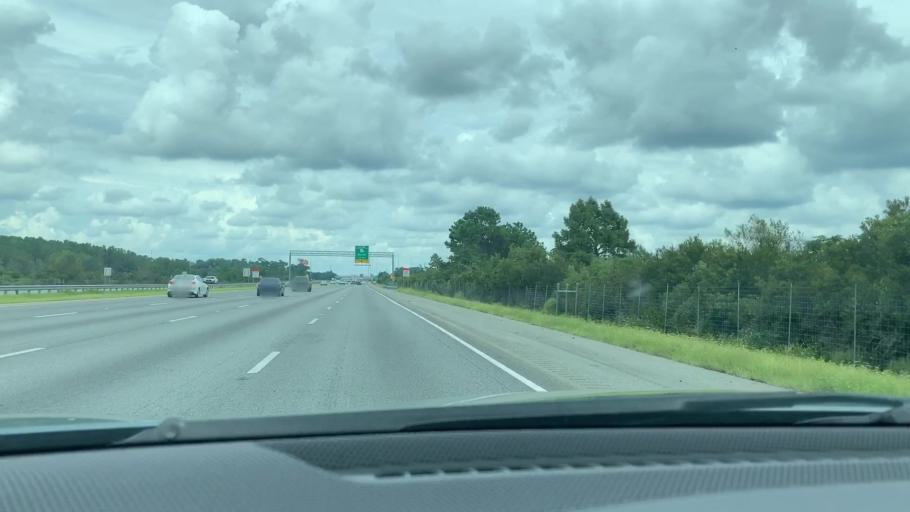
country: US
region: Georgia
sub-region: McIntosh County
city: Darien
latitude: 31.3828
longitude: -81.4522
